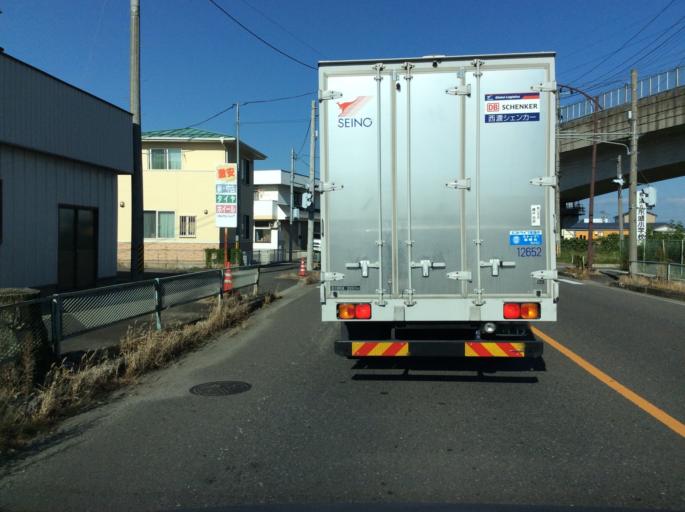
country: JP
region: Fukushima
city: Koriyama
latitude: 37.3662
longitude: 140.3779
